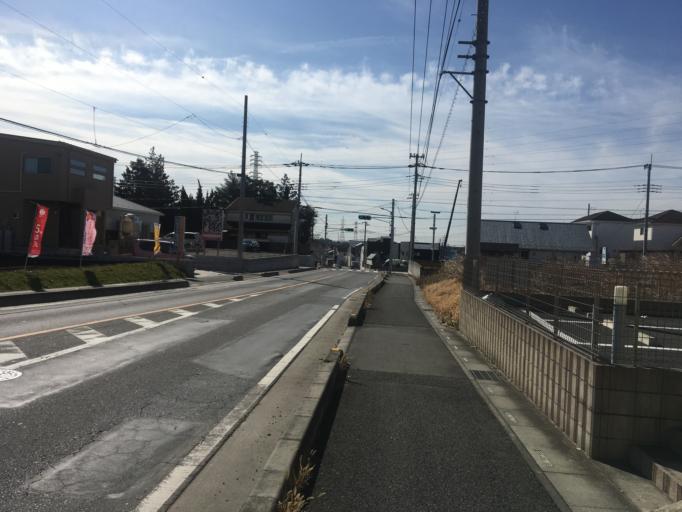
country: JP
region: Saitama
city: Sakado
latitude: 35.9976
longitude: 139.4006
